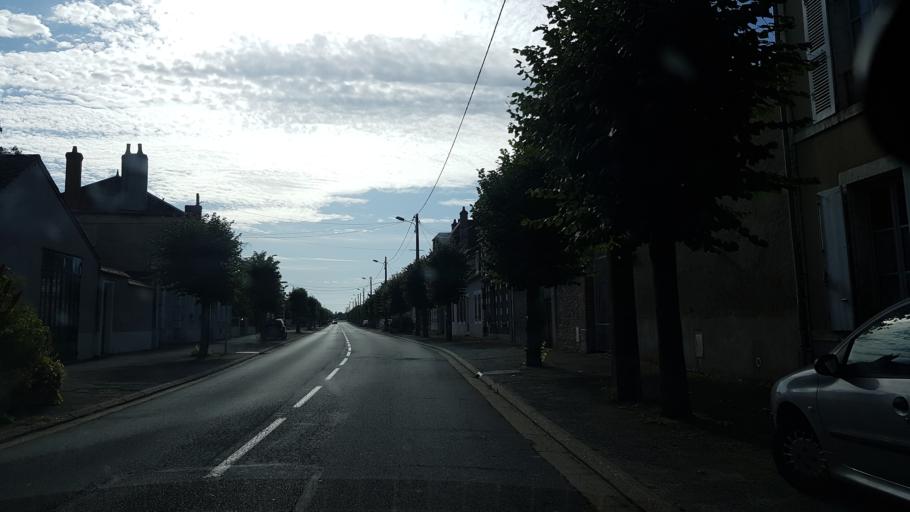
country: FR
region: Centre
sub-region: Departement du Loiret
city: Bonny-sur-Loire
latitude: 47.5583
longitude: 2.8412
